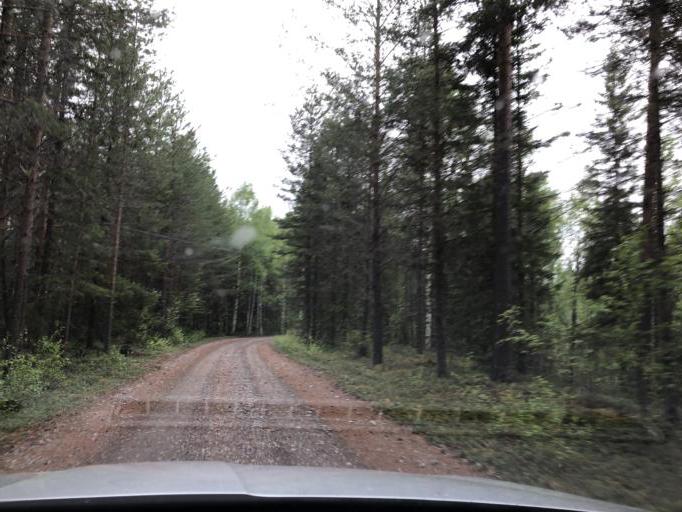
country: SE
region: Norrbotten
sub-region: Pitea Kommun
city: Roknas
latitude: 65.3956
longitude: 21.2659
